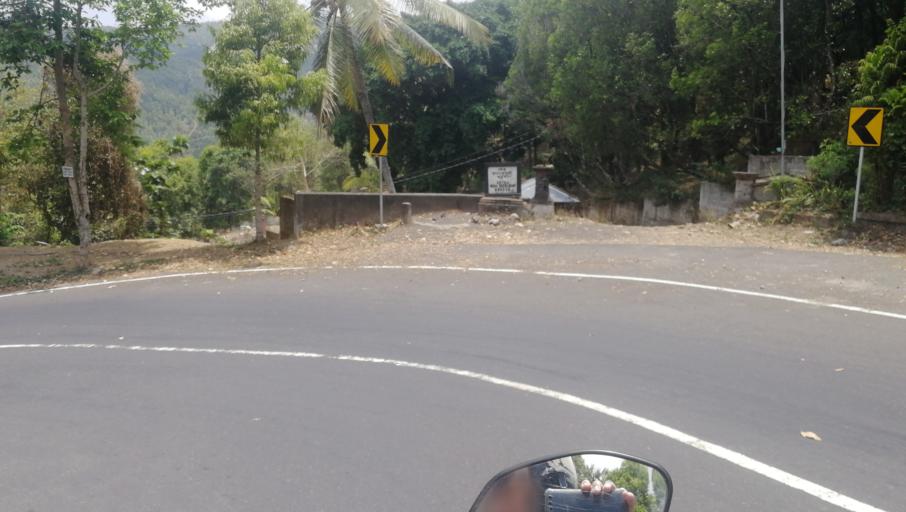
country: ID
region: Bali
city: Munduk
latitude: -8.2643
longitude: 115.0469
